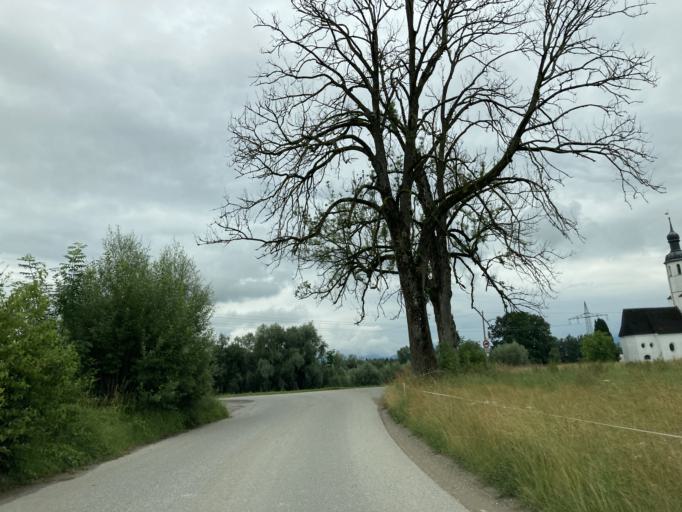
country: DE
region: Bavaria
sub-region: Upper Bavaria
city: Stephanskirchen
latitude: 47.8704
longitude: 12.1654
